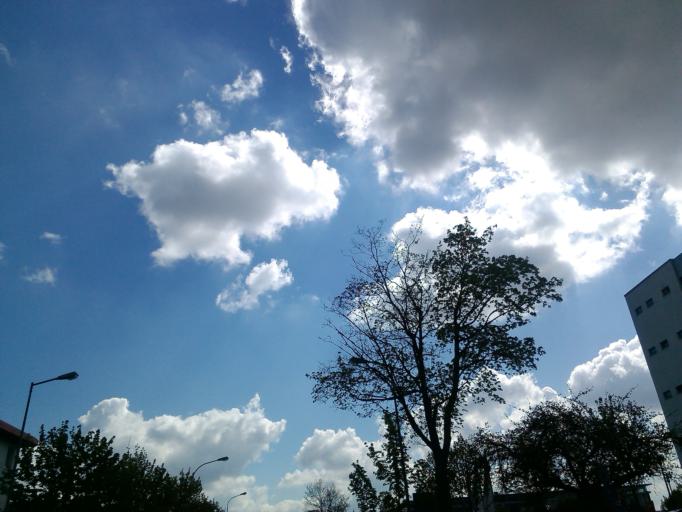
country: DE
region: Bavaria
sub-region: Swabia
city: Stadtbergen
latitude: 48.3860
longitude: 10.8469
